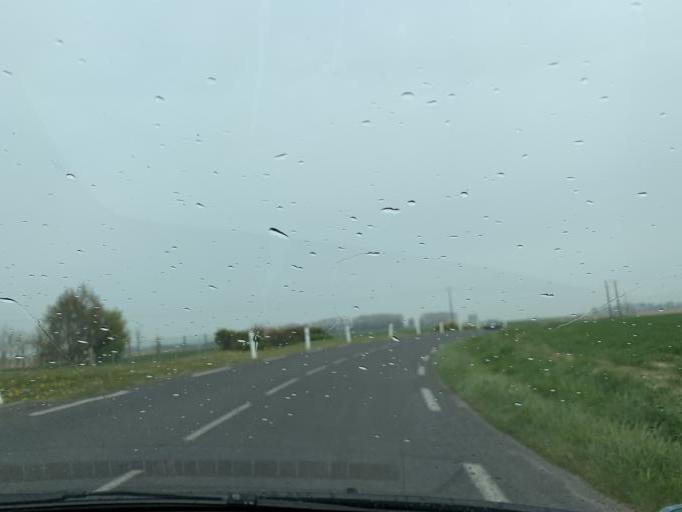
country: FR
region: Haute-Normandie
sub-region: Departement de la Seine-Maritime
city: Cany-Barville
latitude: 49.7894
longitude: 0.6562
